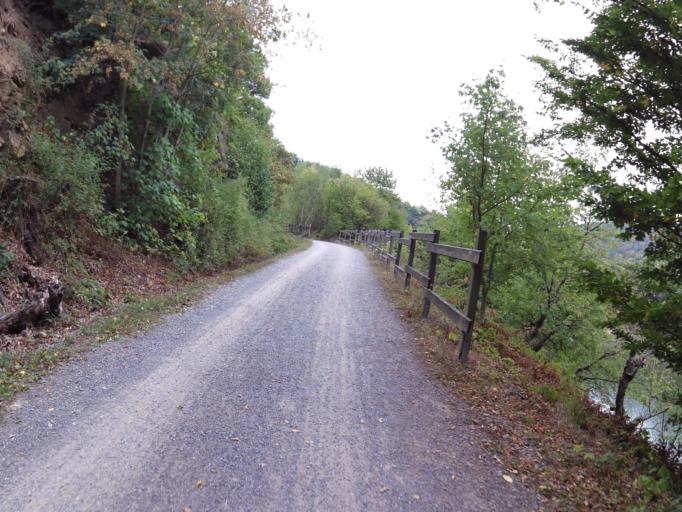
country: DE
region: North Rhine-Westphalia
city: Heimbach
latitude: 50.5976
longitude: 6.4506
